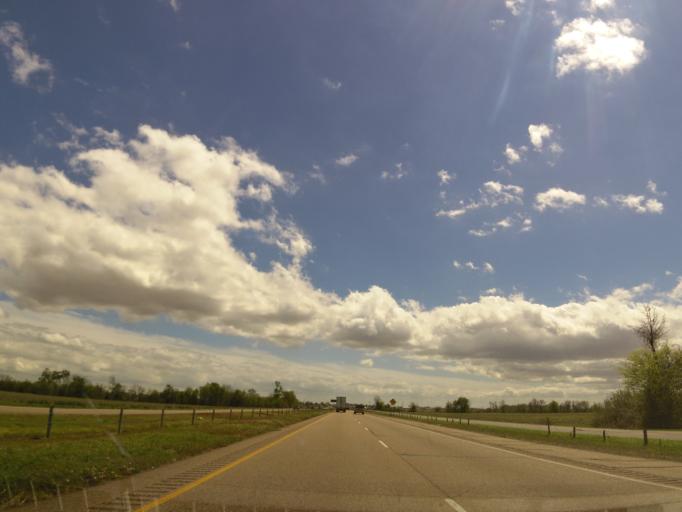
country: US
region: Arkansas
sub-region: Crittenden County
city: Marion
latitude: 35.2512
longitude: -90.2220
